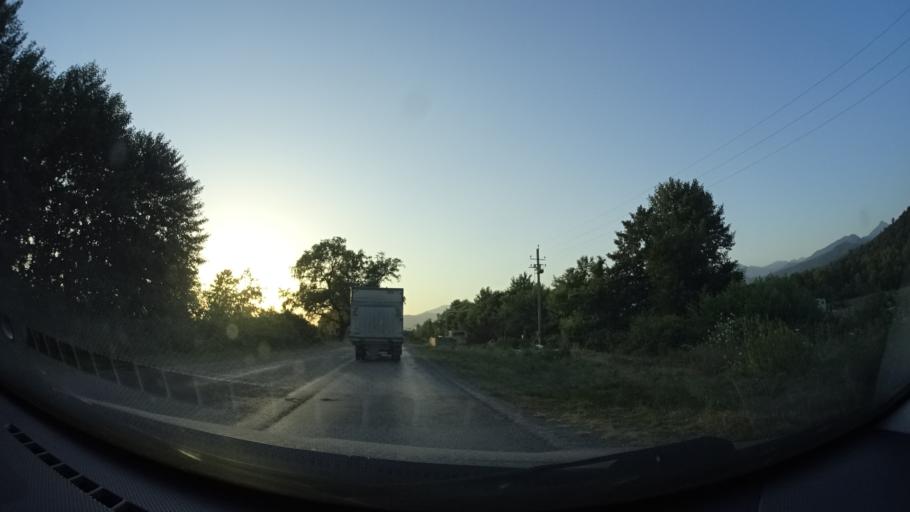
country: GE
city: Bagdadi
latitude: 41.8597
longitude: 46.0241
